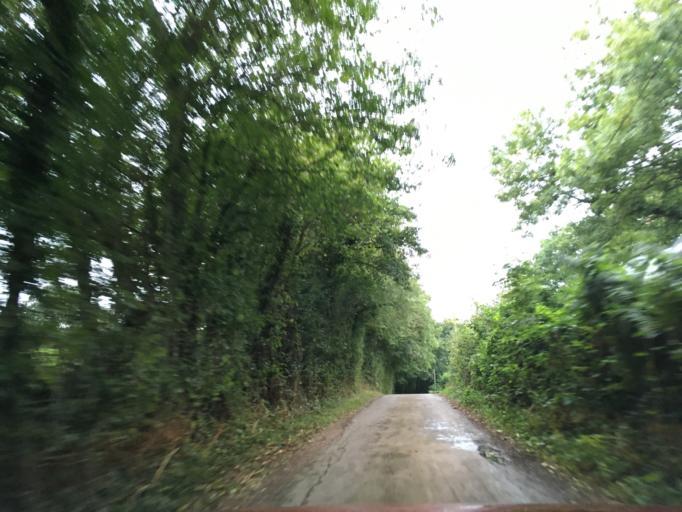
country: GB
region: Wales
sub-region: Monmouthshire
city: Llangybi
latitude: 51.6505
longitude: -2.8785
